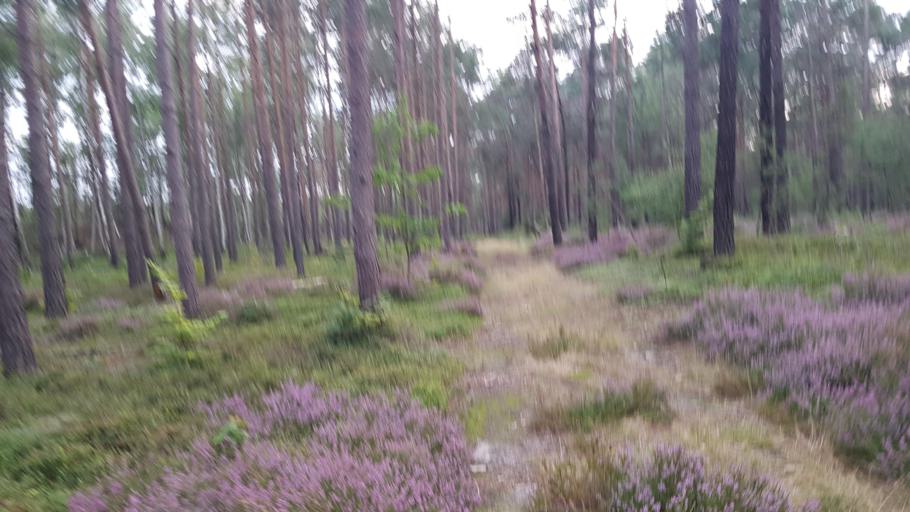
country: DE
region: Brandenburg
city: Trobitz
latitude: 51.6122
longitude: 13.4408
